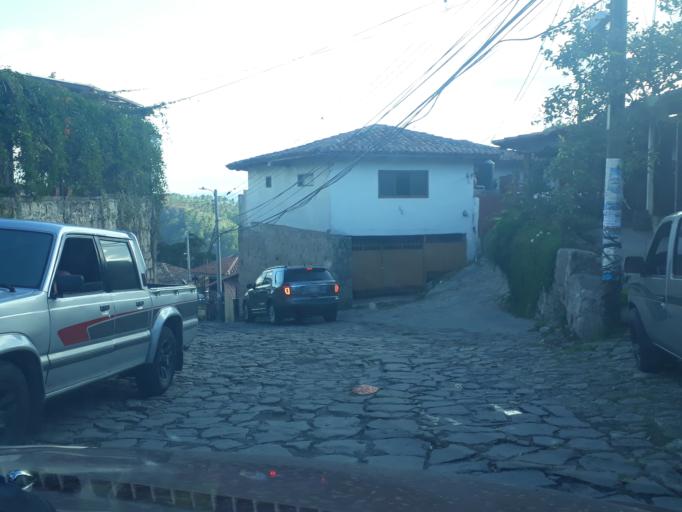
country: HN
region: Francisco Morazan
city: Santa Lucia
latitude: 14.1164
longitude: -87.1132
